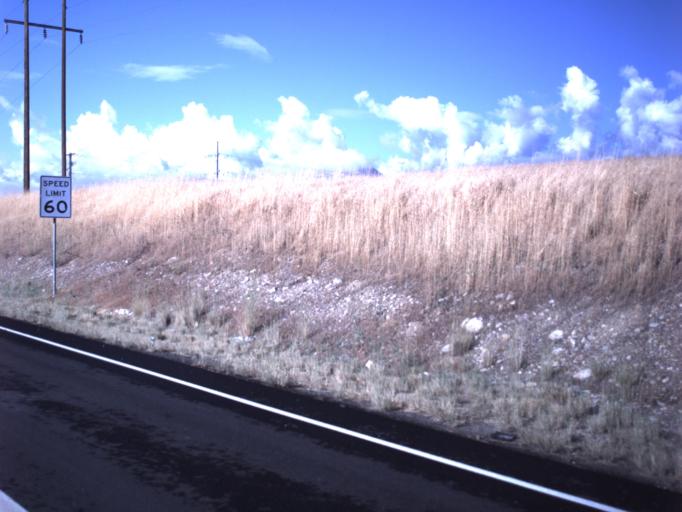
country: US
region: Utah
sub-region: Salt Lake County
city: Oquirrh
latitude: 40.5980
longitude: -112.0577
